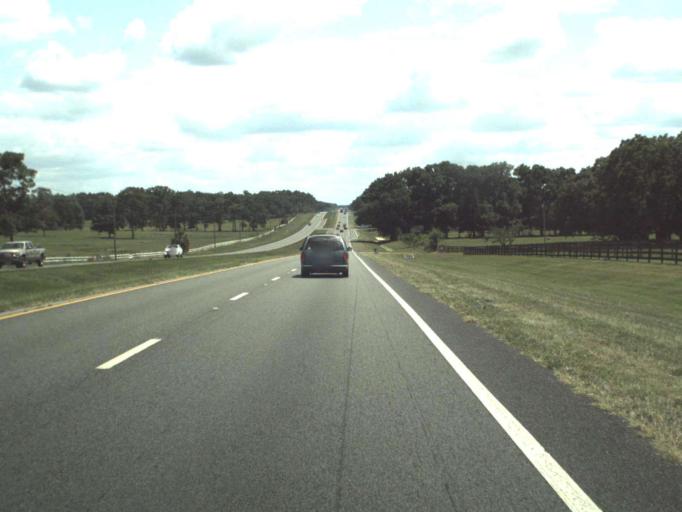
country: US
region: Florida
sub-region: Marion County
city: Ocala
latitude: 29.2866
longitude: -82.1520
